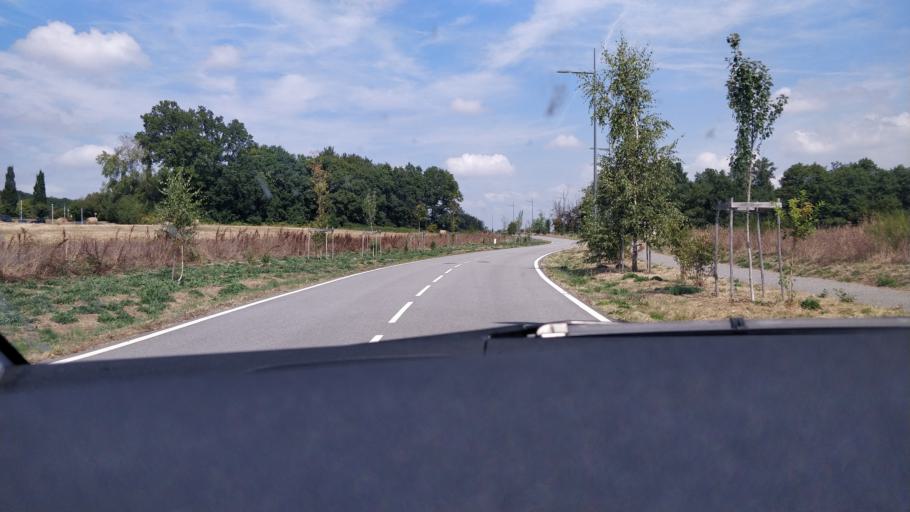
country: FR
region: Limousin
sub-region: Departement de la Haute-Vienne
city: Le Palais-sur-Vienne
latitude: 45.8610
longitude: 1.2988
